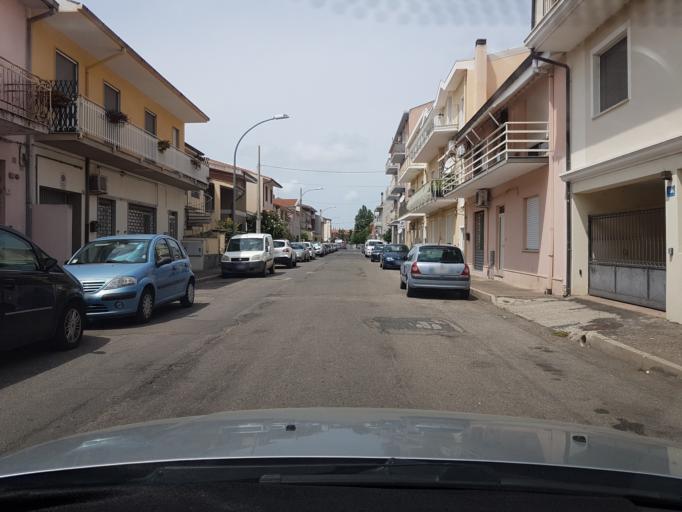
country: IT
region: Sardinia
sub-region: Provincia di Oristano
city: Oristano
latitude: 39.9105
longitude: 8.5939
